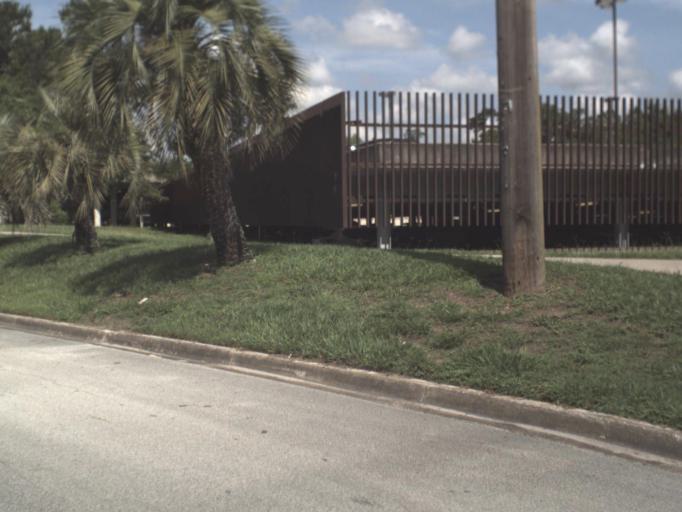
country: US
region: Florida
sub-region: Alachua County
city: Gainesville
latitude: 29.6382
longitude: -82.3462
